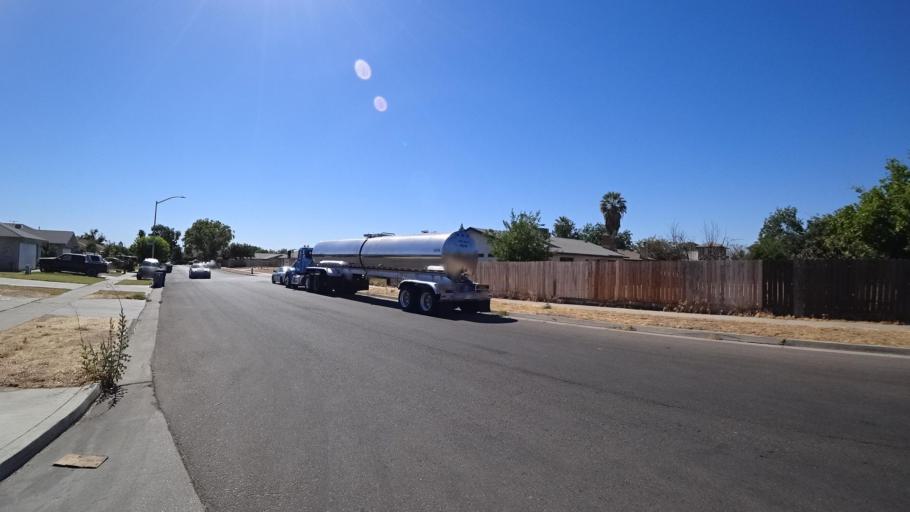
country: US
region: California
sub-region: Fresno County
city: Fresno
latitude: 36.7215
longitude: -119.7947
